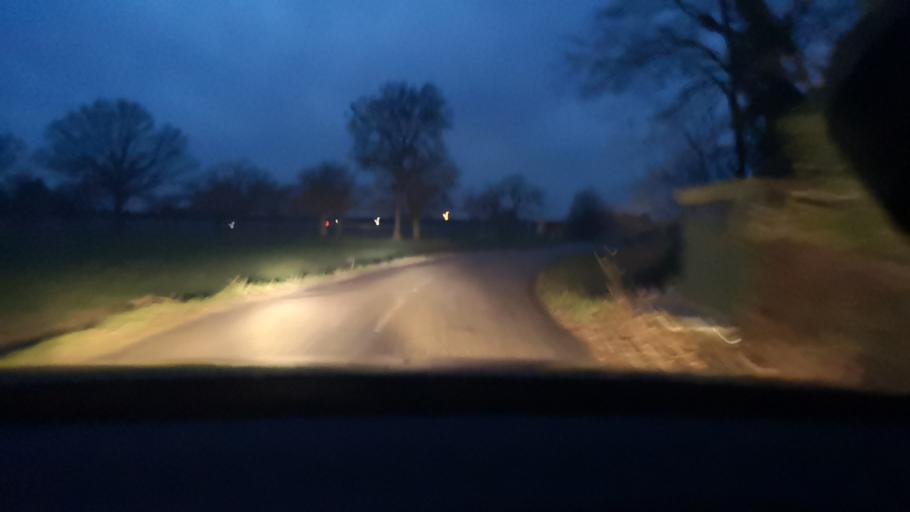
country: FR
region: Bourgogne
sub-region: Departement de Saone-et-Loire
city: Champforgeuil
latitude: 46.8447
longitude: 4.8338
